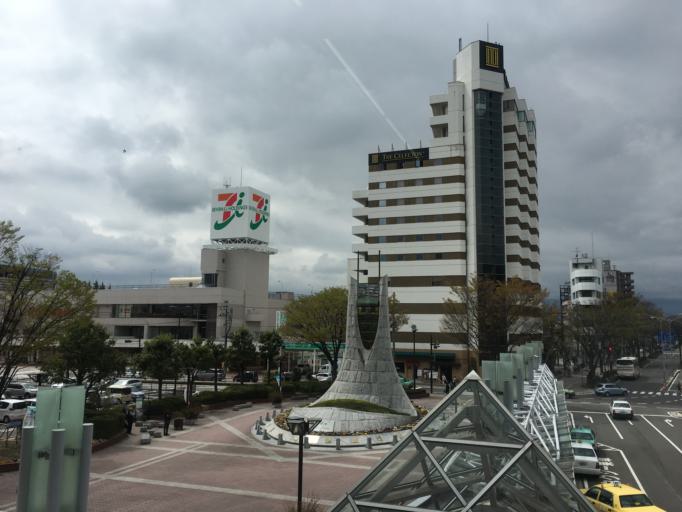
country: JP
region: Fukushima
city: Fukushima-shi
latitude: 37.7549
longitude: 140.4583
